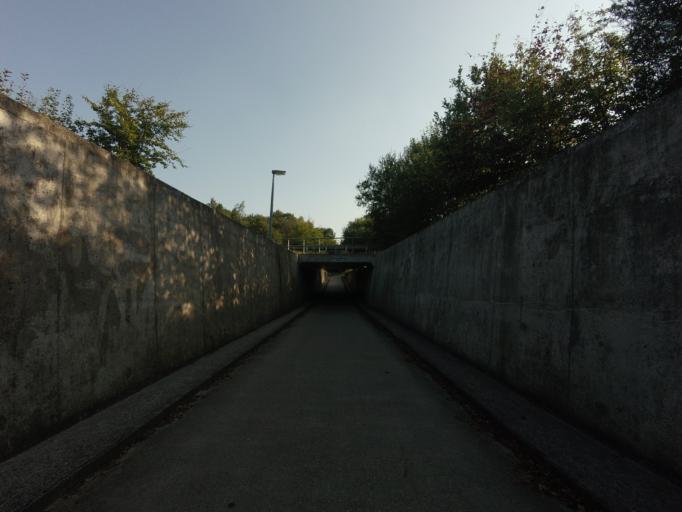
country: NL
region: Drenthe
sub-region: Gemeente Tynaarlo
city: Vries
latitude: 53.1398
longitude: 6.4891
